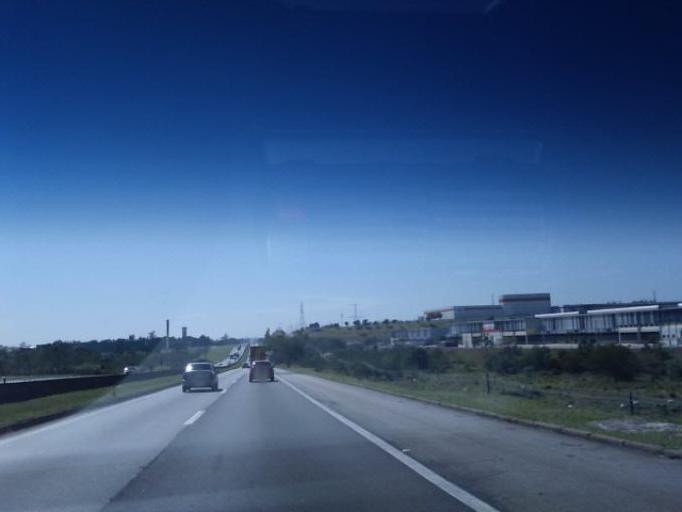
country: BR
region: Sao Paulo
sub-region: Cacapava
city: Cacapava
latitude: -23.1398
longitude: -45.7609
